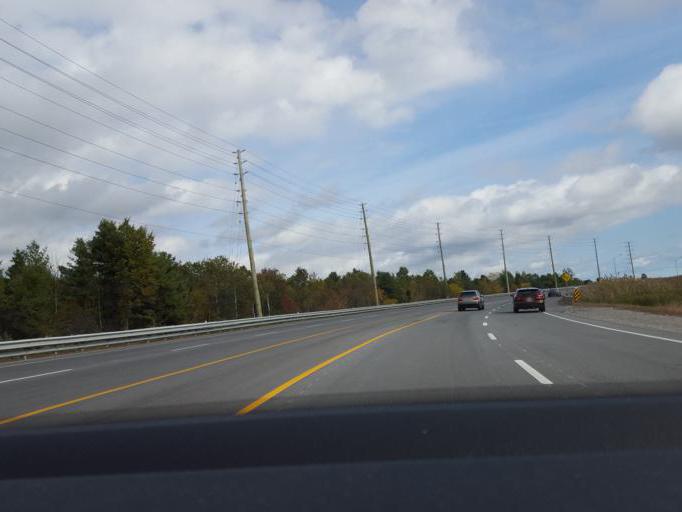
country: CA
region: Ontario
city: Pickering
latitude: 43.8882
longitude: -79.0852
